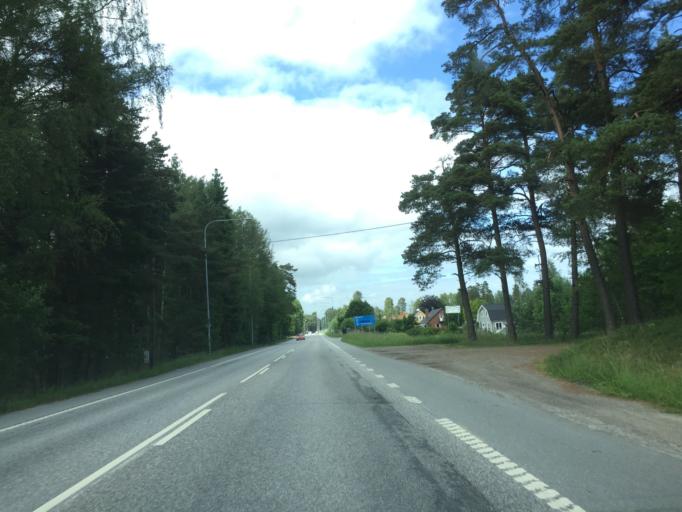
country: SE
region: OErebro
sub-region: Orebro Kommun
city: Orebro
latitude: 59.2211
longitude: 15.1455
